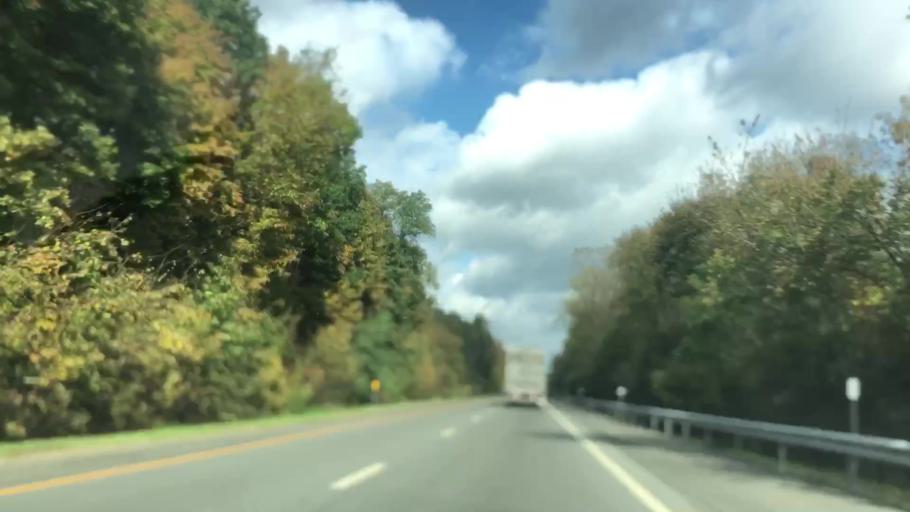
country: US
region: New York
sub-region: Orange County
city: Vails Gate
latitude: 41.4731
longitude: -74.0741
